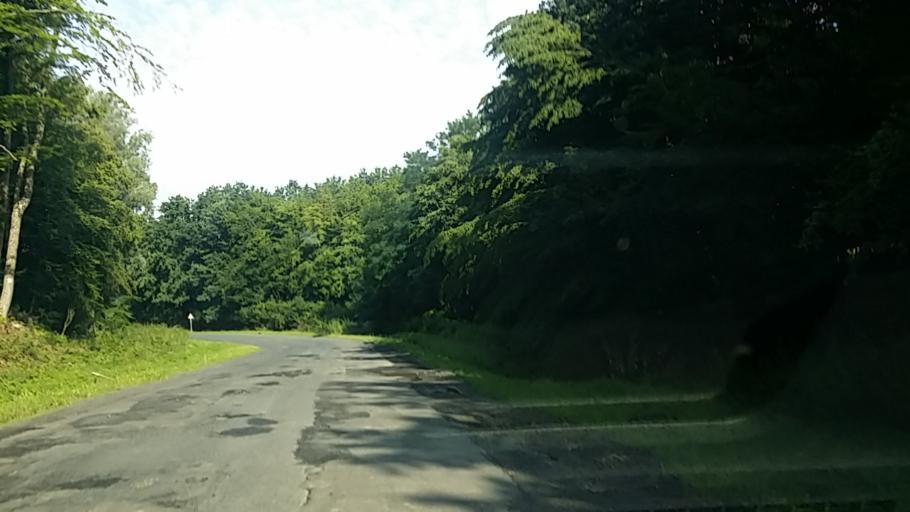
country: HU
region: Zala
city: Letenye
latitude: 46.5312
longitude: 16.7092
